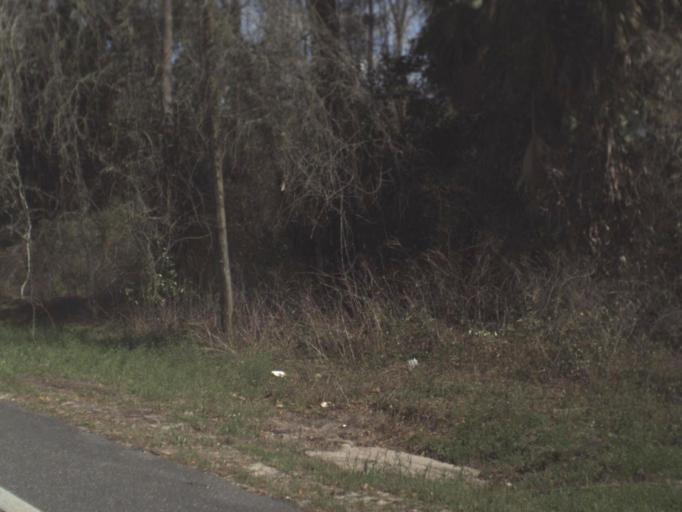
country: US
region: Florida
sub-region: Wakulla County
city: Crawfordville
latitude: 30.1376
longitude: -84.3878
